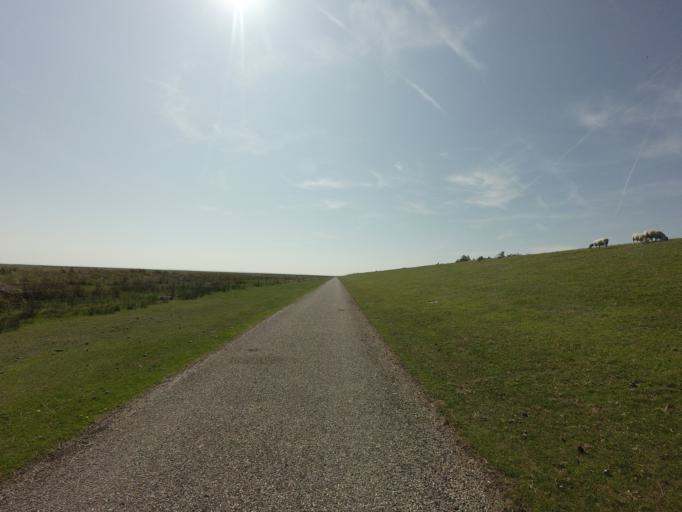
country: NL
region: Friesland
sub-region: Gemeente Schiermonnikoog
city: Schiermonnikoog
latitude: 53.4790
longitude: 6.2106
